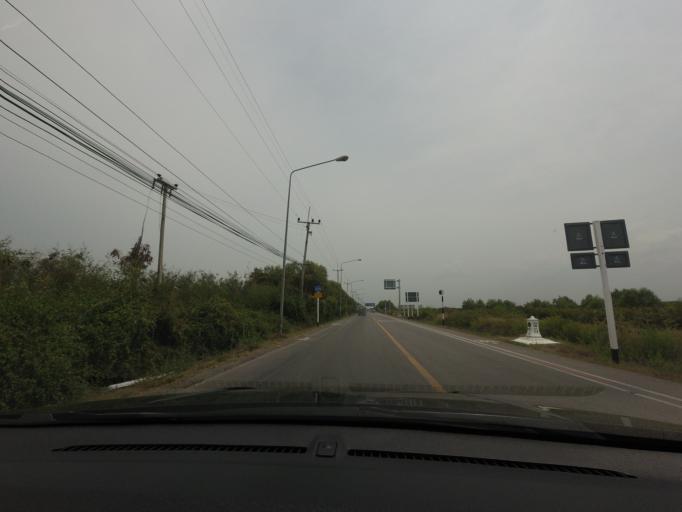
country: TH
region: Ratchaburi
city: Pak Tho
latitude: 13.3289
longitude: 99.9267
